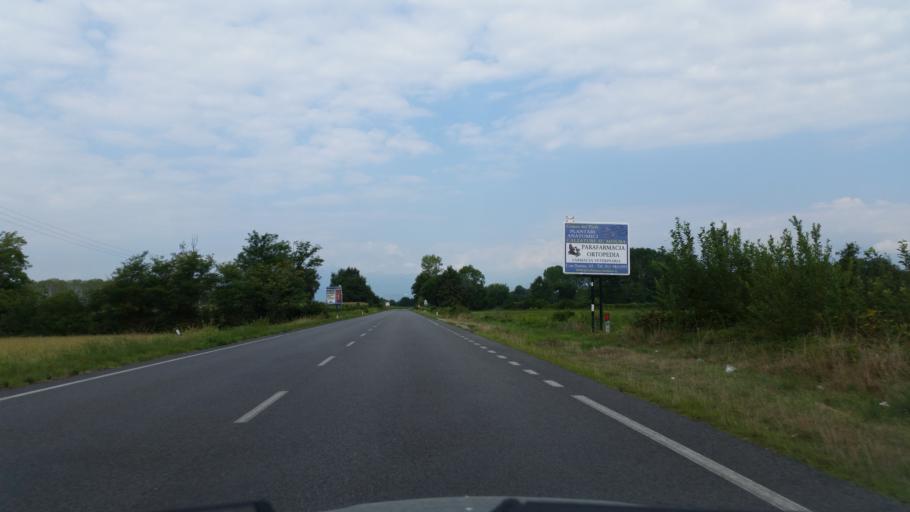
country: IT
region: Piedmont
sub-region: Provincia di Torino
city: Orio Canavese
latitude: 45.3114
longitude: 7.8438
